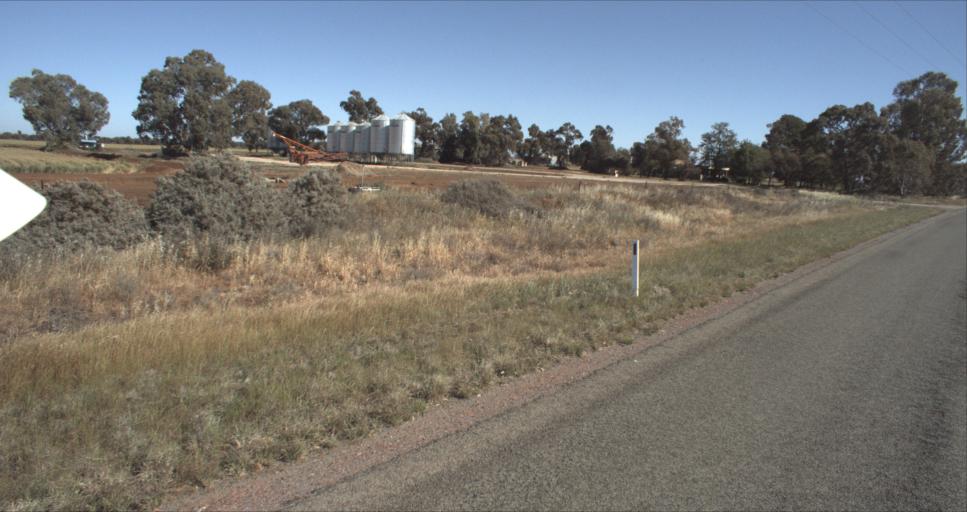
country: AU
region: New South Wales
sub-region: Leeton
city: Leeton
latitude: -34.5564
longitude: 146.2663
